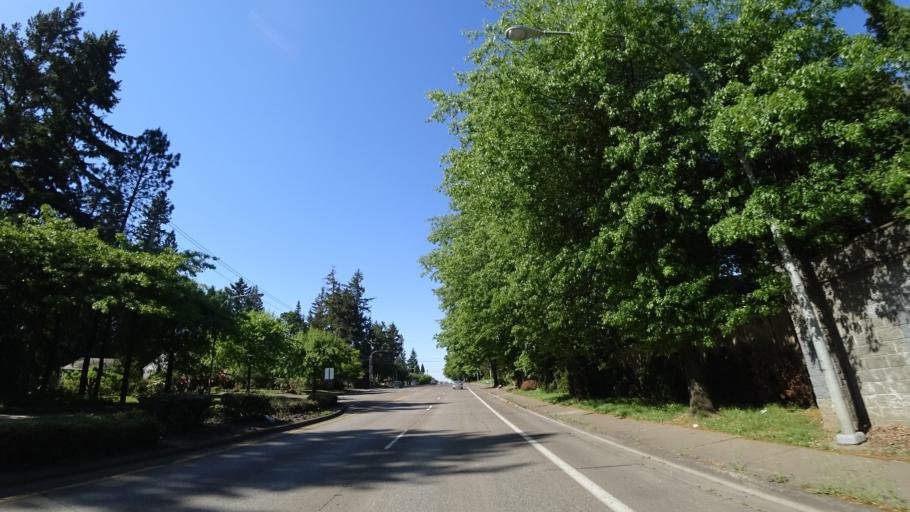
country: US
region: Oregon
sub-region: Washington County
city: Aloha
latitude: 45.5085
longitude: -122.8673
